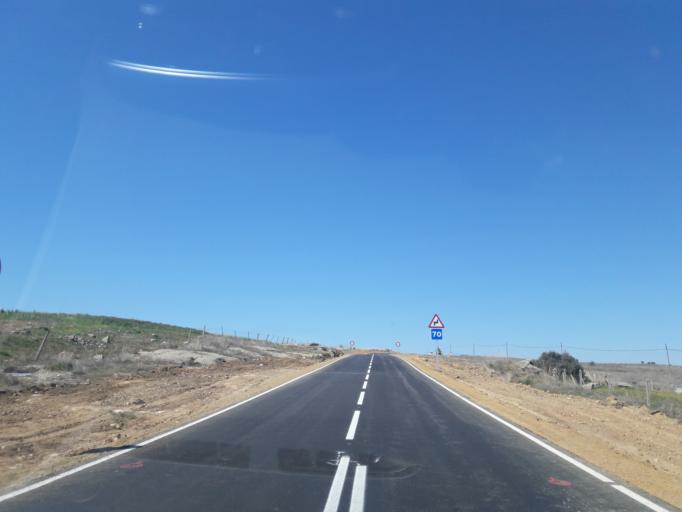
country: ES
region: Castille and Leon
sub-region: Provincia de Salamanca
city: Valdemierque
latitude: 40.8234
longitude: -5.5679
